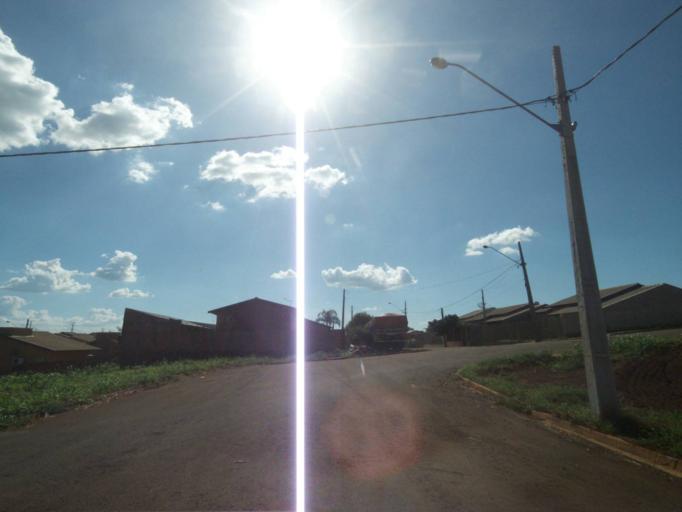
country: BR
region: Parana
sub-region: Sertanopolis
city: Sertanopolis
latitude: -23.0445
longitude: -50.8163
